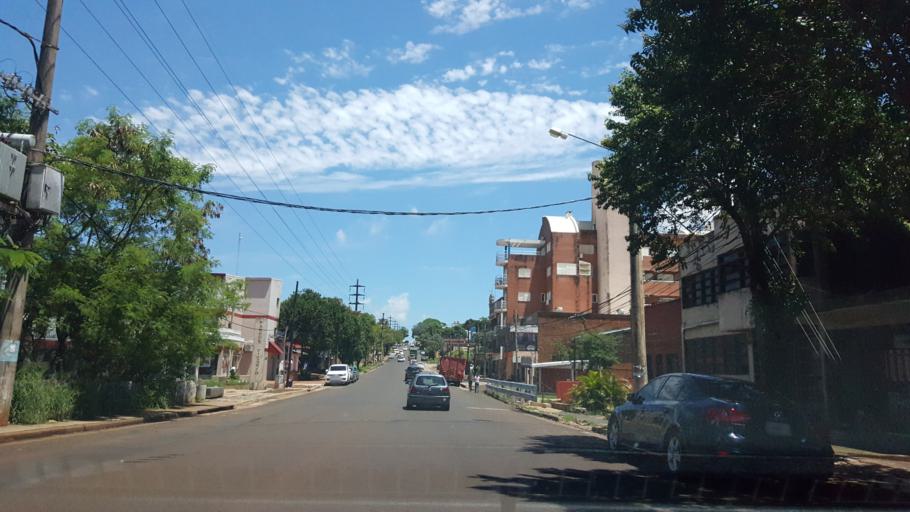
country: AR
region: Misiones
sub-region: Departamento de Capital
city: Posadas
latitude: -27.3800
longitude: -55.8917
